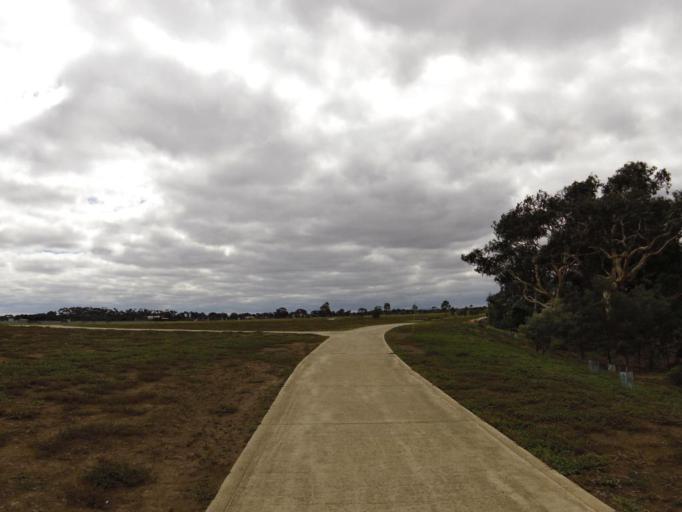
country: AU
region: Victoria
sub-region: Wyndham
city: Tarneit
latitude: -37.8822
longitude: 144.6397
